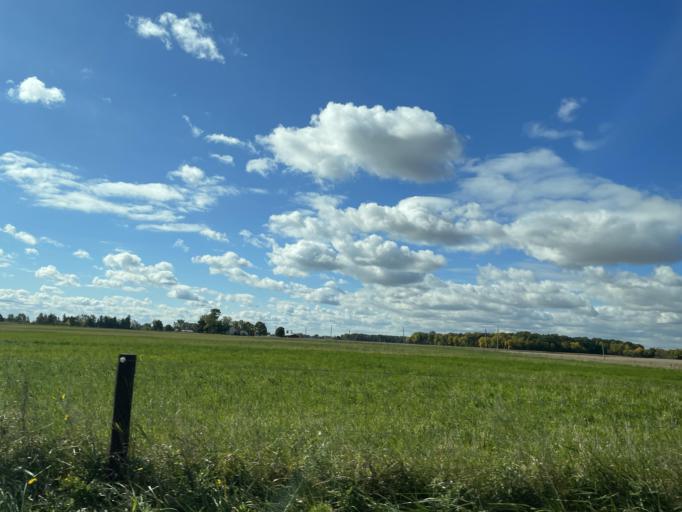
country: US
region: Indiana
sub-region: Whitley County
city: Churubusco
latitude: 41.1249
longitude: -85.2834
